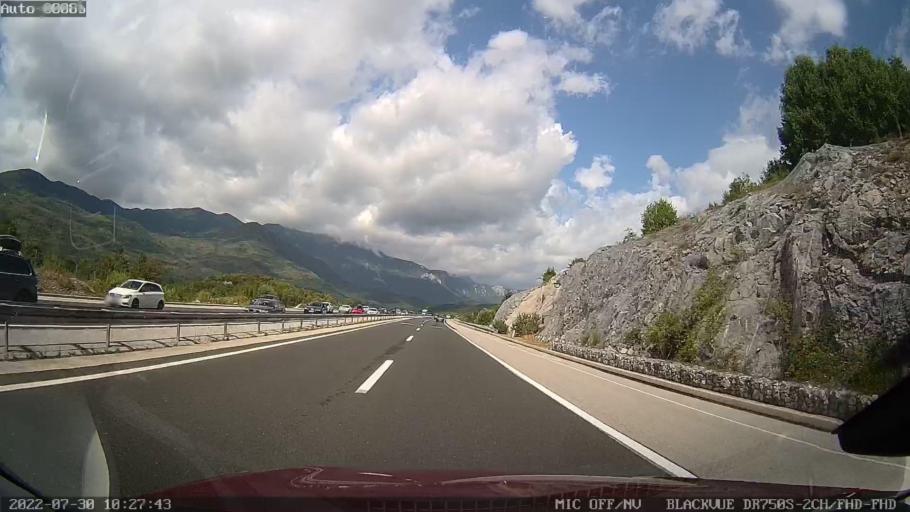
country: HR
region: Zadarska
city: Obrovac
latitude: 44.3313
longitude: 15.6633
